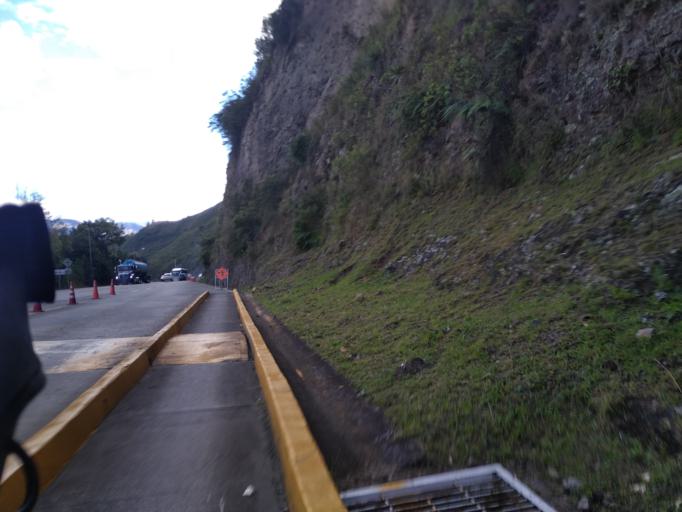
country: CO
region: Narino
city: Tangua
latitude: 1.0873
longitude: -77.4089
